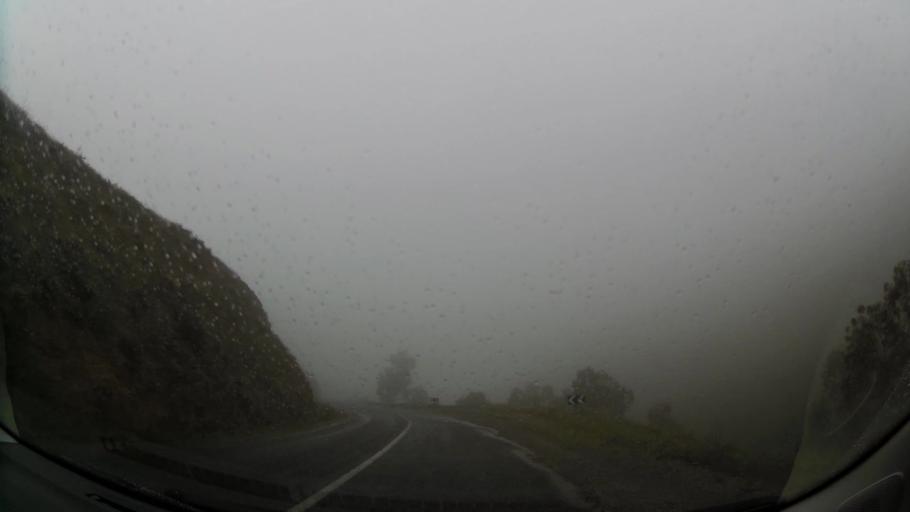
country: MA
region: Oriental
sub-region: Nador
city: Boudinar
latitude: 35.1060
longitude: -3.5592
